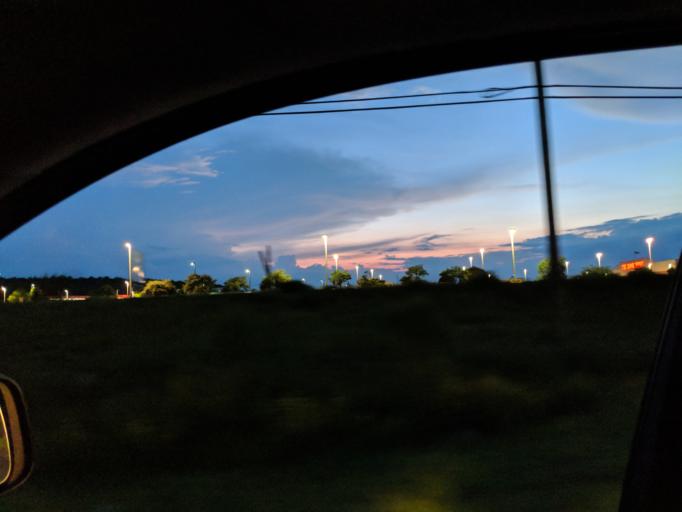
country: US
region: Florida
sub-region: Nassau County
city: Yulee
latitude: 30.6279
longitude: -81.5471
